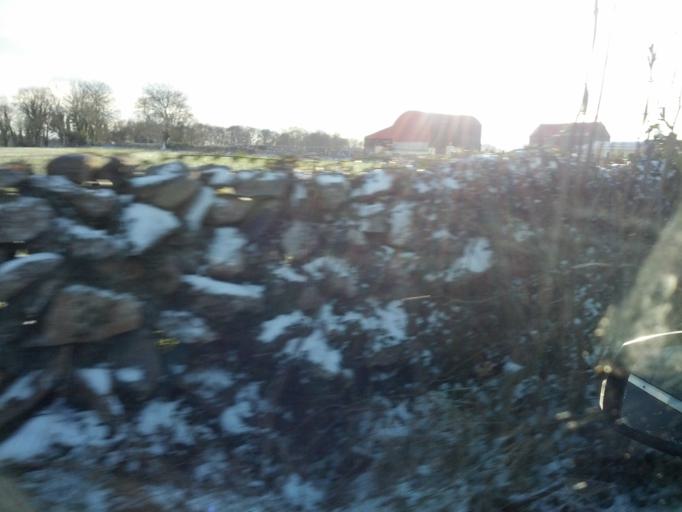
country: IE
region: Connaught
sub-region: County Galway
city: Gort
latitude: 53.1708
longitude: -8.7999
